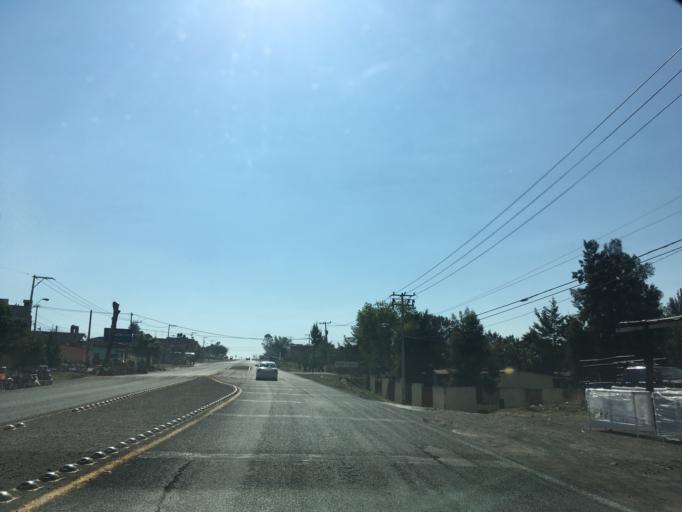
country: MX
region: Michoacan
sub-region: Morelia
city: La Aldea
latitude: 19.7368
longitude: -101.1158
